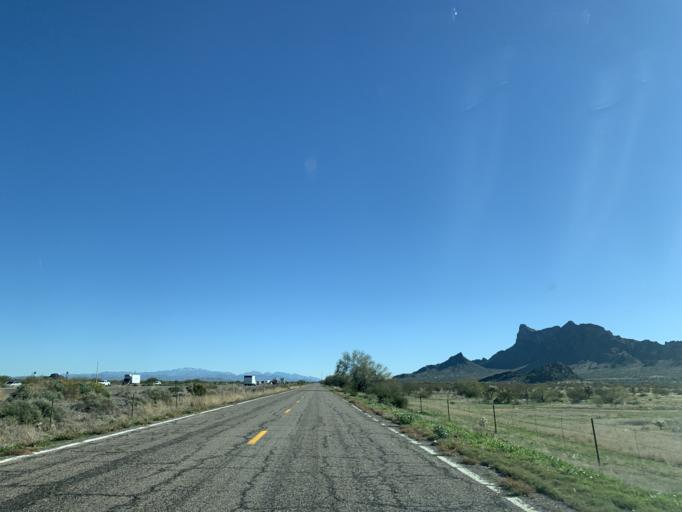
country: US
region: Arizona
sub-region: Pinal County
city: Eloy
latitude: 32.6698
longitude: -111.4262
